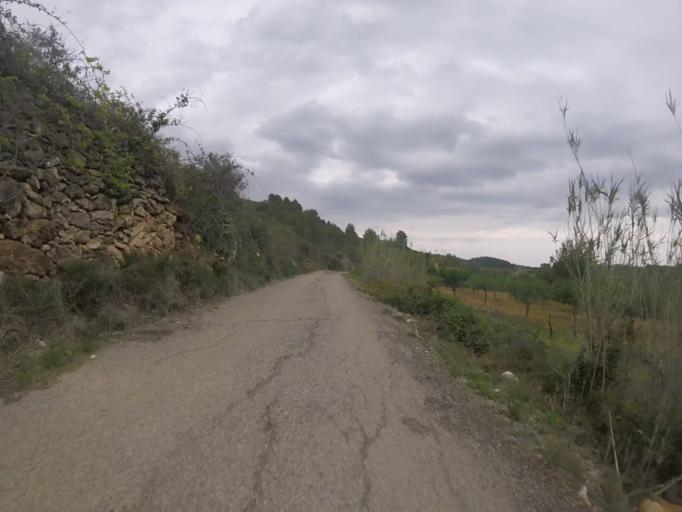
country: ES
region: Valencia
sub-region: Provincia de Castello
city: Sarratella
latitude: 40.2684
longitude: 0.0697
